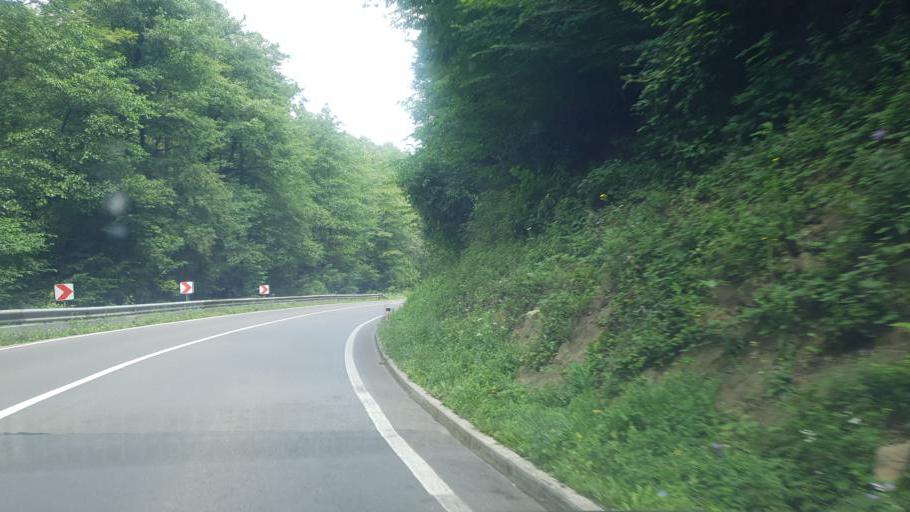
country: SI
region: Ilirska Bistrica
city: Ilirska Bistrica
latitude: 45.5160
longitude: 14.2527
